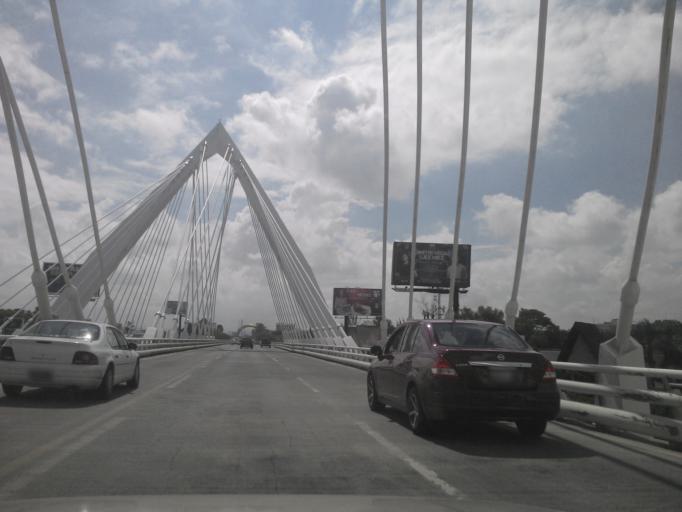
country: MX
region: Jalisco
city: Guadalajara
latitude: 20.6650
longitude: -103.3942
